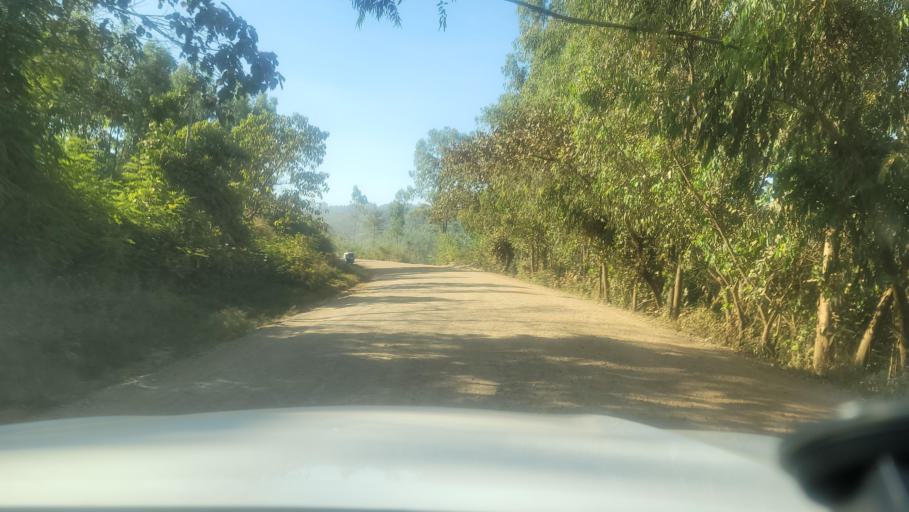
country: ET
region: Oromiya
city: Agaro
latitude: 7.8371
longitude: 36.5420
